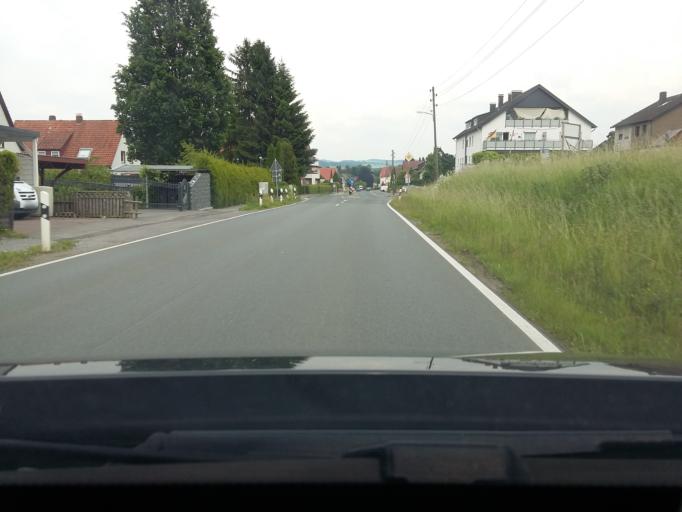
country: DE
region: North Rhine-Westphalia
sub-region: Regierungsbezirk Detmold
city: Bad Salzuflen
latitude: 52.1016
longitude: 8.7847
